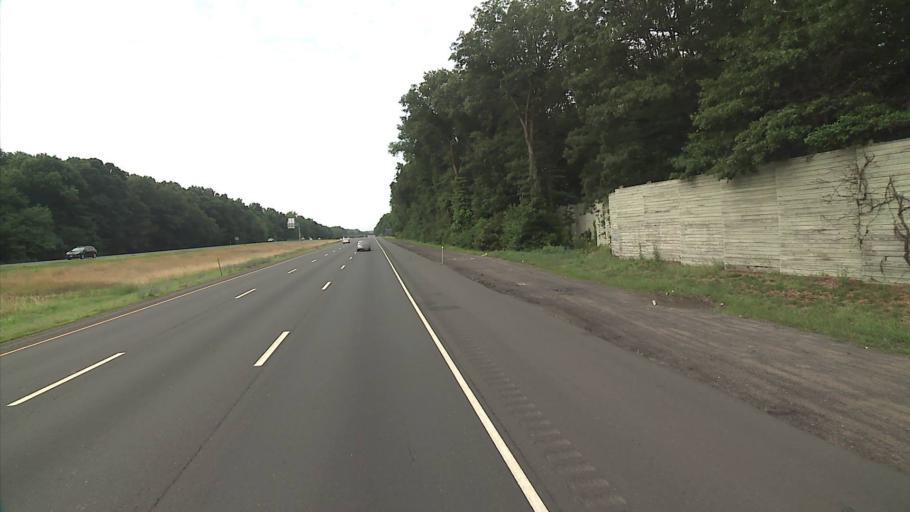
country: US
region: Connecticut
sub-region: Hartford County
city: Plainville
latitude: 41.6567
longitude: -72.8522
